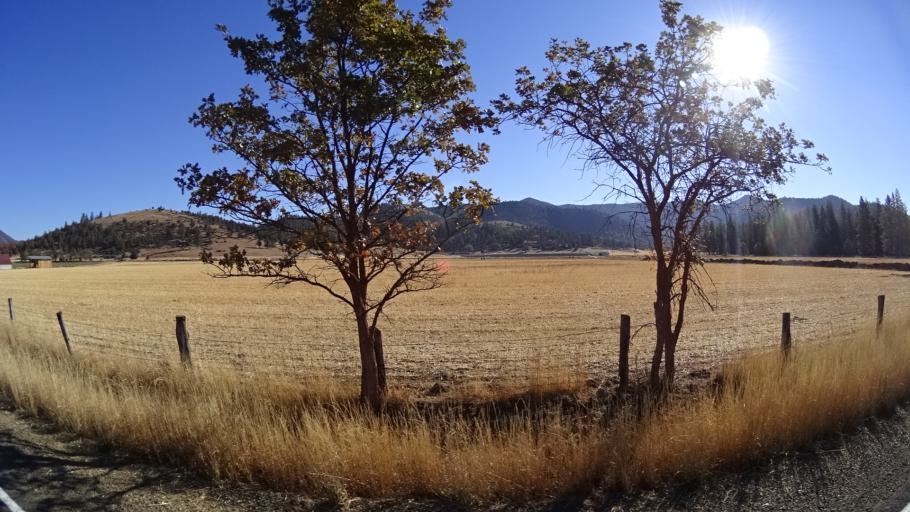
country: US
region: California
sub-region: Siskiyou County
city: Yreka
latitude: 41.5505
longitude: -122.8289
